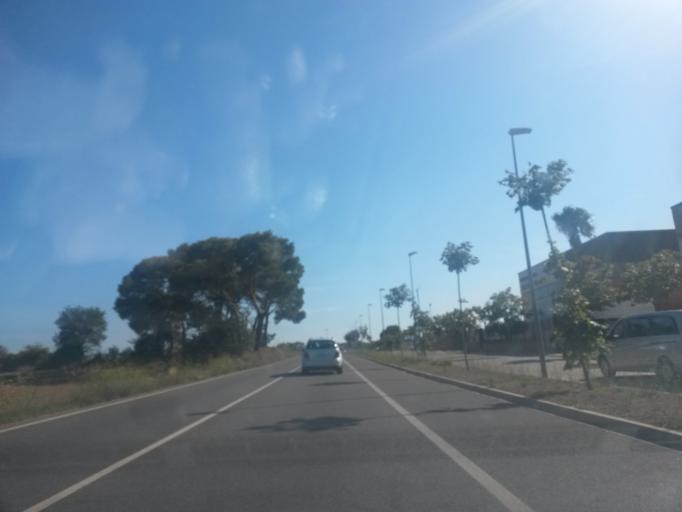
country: ES
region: Catalonia
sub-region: Provincia de Girona
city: Palafrugell
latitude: 41.9348
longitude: 3.1597
